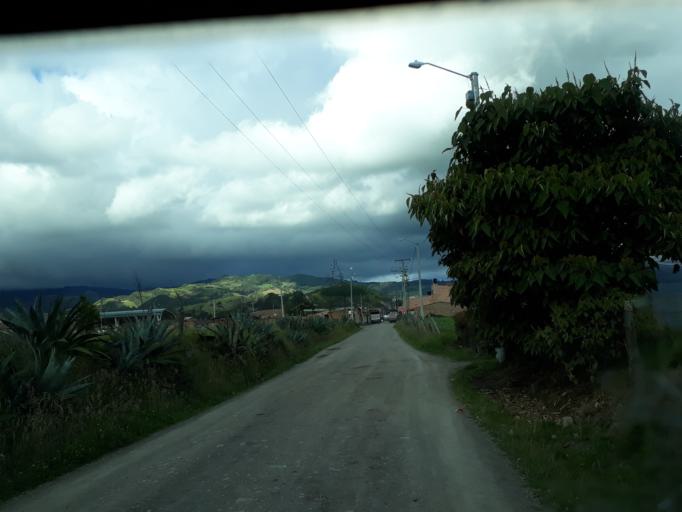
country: CO
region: Cundinamarca
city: Carmen de Carupa
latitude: 5.3496
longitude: -73.9063
